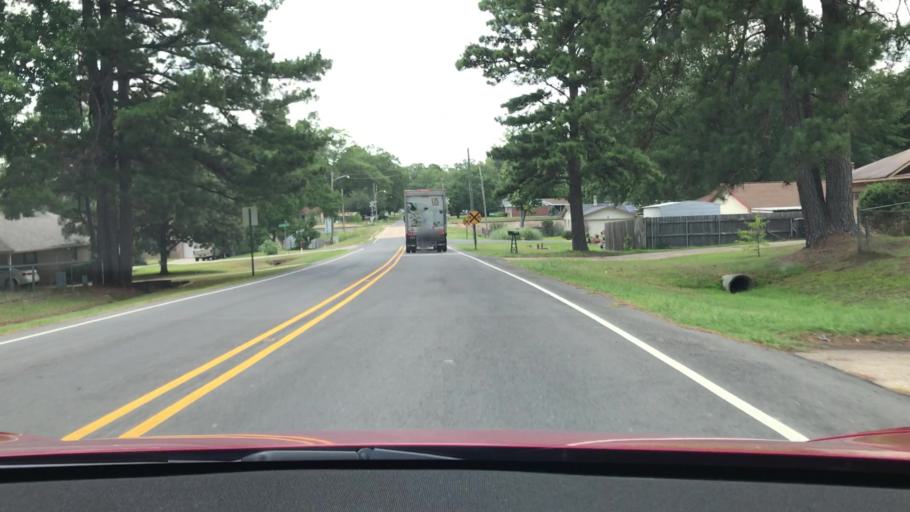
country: US
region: Louisiana
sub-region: De Soto Parish
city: Stonewall
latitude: 32.3943
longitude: -93.7984
